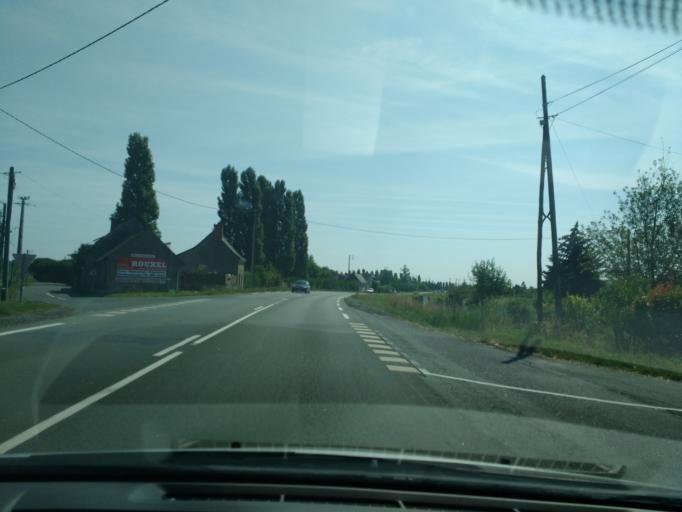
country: FR
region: Pays de la Loire
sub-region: Departement de Maine-et-Loire
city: Maze
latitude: 47.4656
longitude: -0.2950
